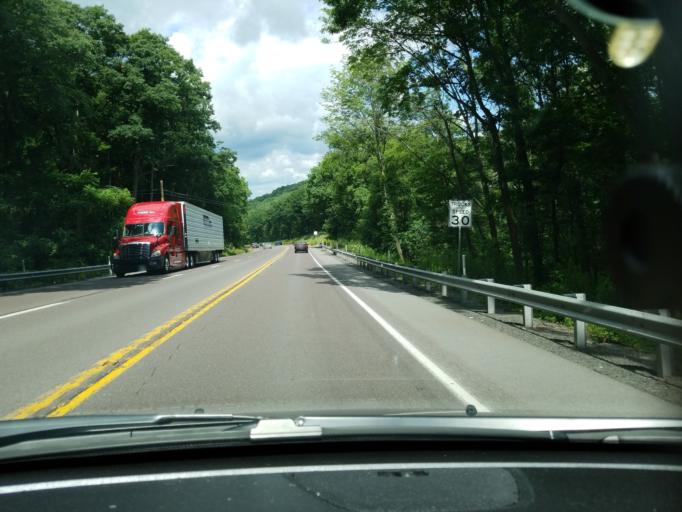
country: US
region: Pennsylvania
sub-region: Northumberland County
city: Elysburg
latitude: 40.8494
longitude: -76.5305
